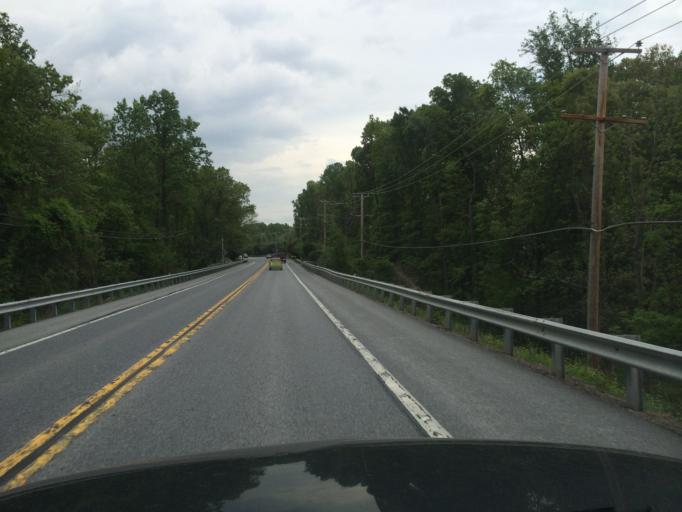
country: US
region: Maryland
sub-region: Carroll County
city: Eldersburg
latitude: 39.4215
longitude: -76.9401
